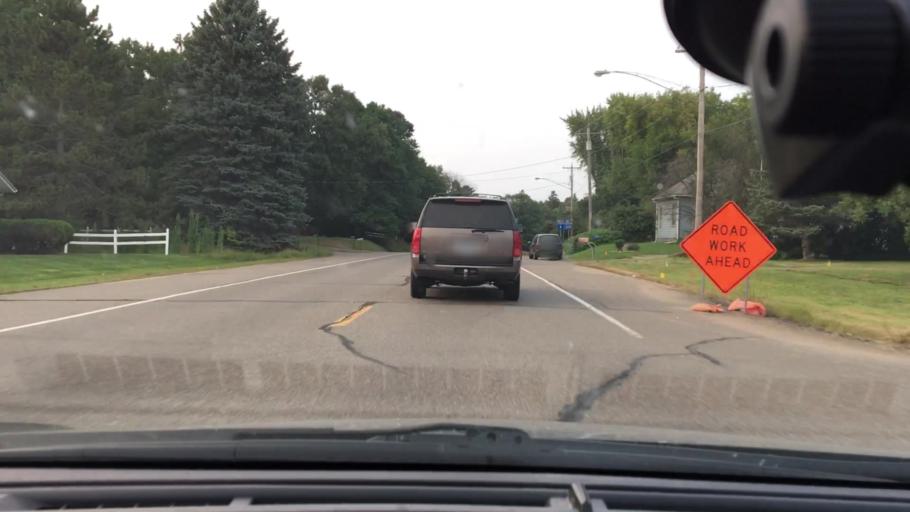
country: US
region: Minnesota
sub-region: Crow Wing County
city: Crosby
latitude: 46.4765
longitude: -93.9014
